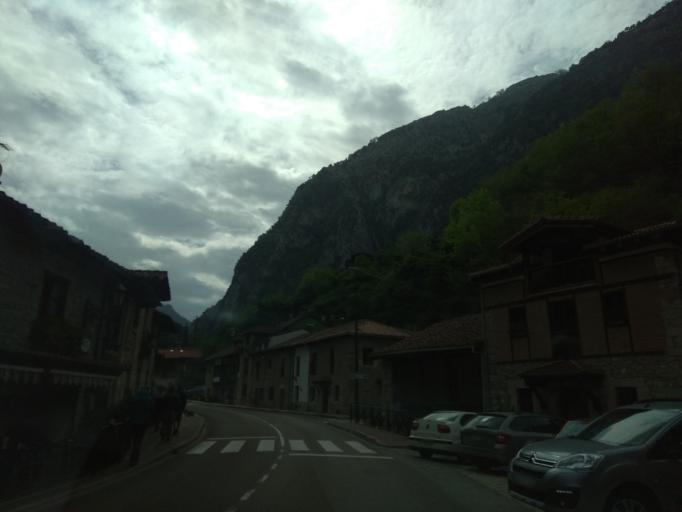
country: ES
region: Cantabria
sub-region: Provincia de Cantabria
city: Tresviso
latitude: 43.2548
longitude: -4.6152
